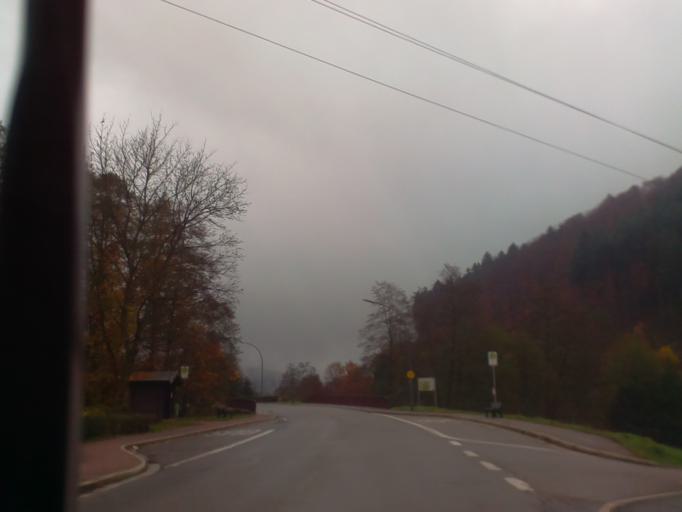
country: DE
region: Baden-Wuerttemberg
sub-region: Karlsruhe Region
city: Heiligkreuzsteinach
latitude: 49.4676
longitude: 8.8012
